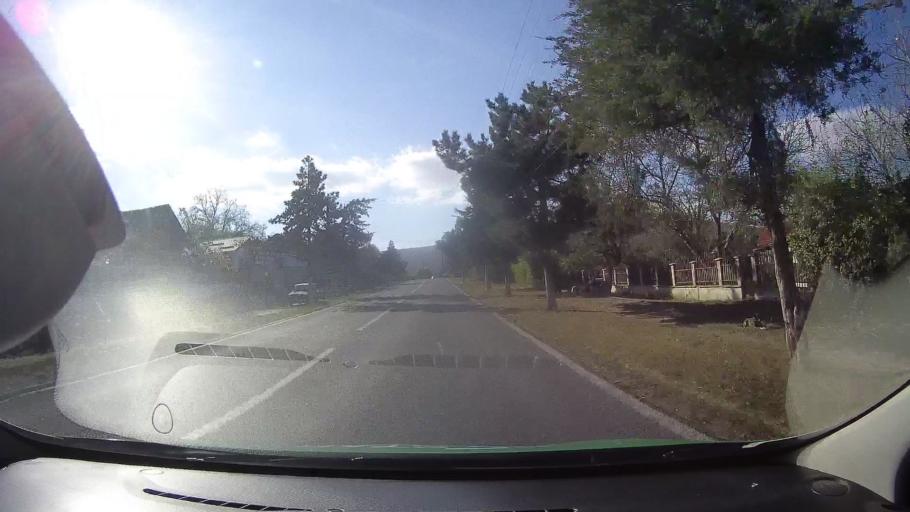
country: RO
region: Tulcea
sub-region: Oras Babadag
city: Babadag
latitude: 44.8801
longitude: 28.6929
